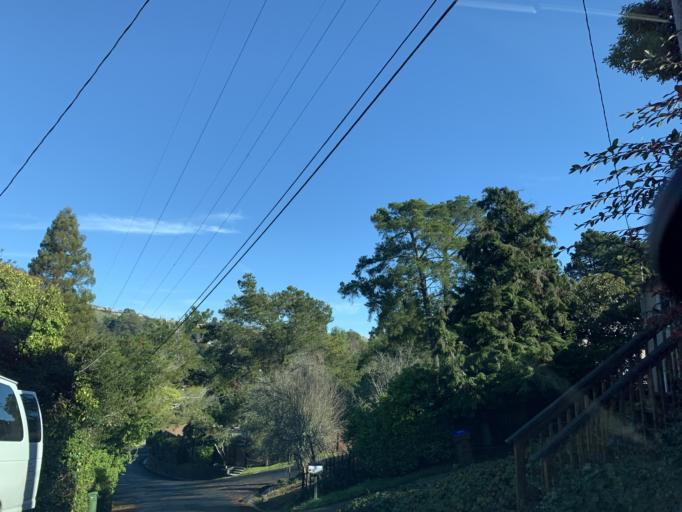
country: US
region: California
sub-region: Marin County
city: Strawberry
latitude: 37.8974
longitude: -122.5126
